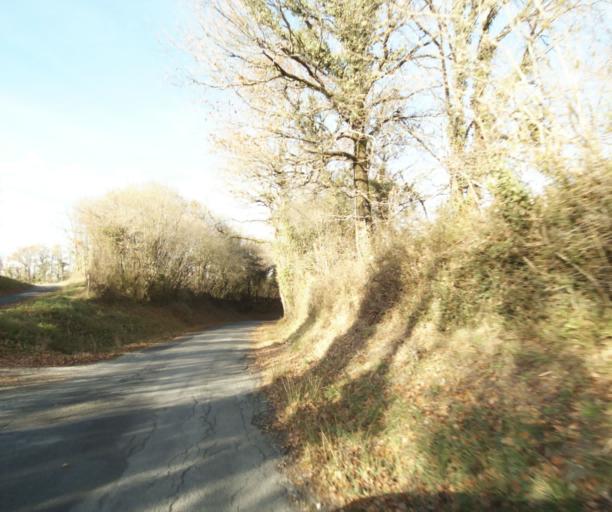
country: FR
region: Poitou-Charentes
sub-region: Departement de la Charente-Maritime
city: Chaniers
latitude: 45.7527
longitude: -0.4979
